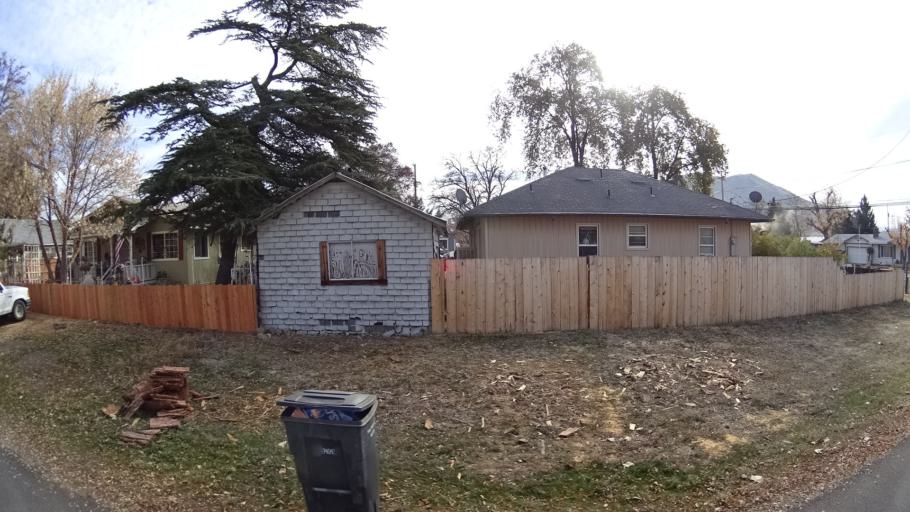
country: US
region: California
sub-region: Siskiyou County
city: Montague
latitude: 41.7262
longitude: -122.5219
